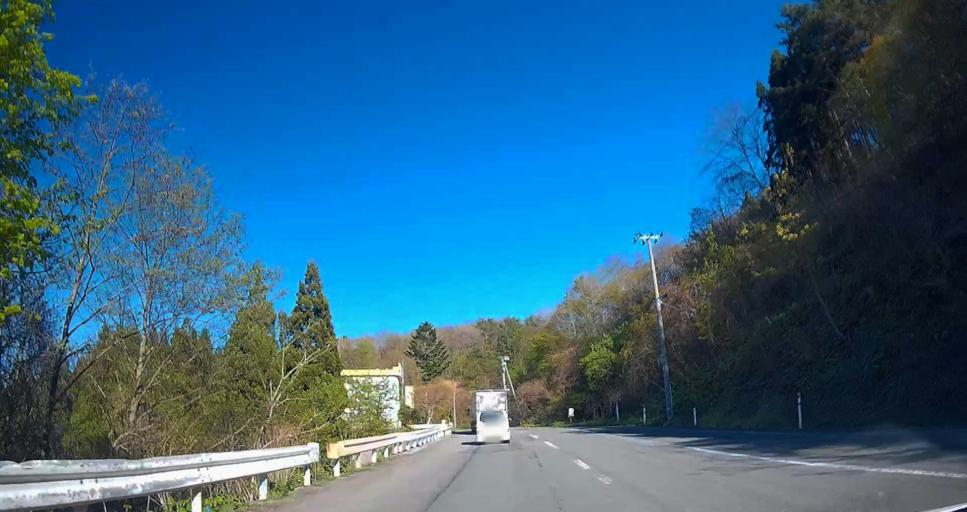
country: JP
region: Aomori
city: Mutsu
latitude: 41.4329
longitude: 141.1358
